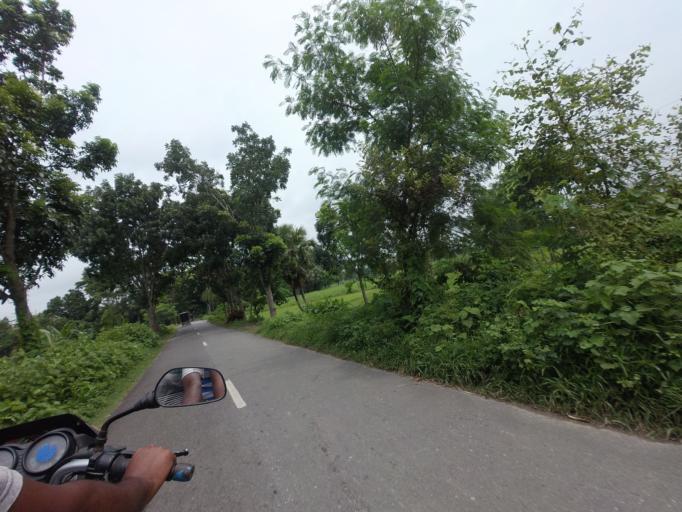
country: BD
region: Khulna
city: Kalia
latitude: 23.0927
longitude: 89.6556
